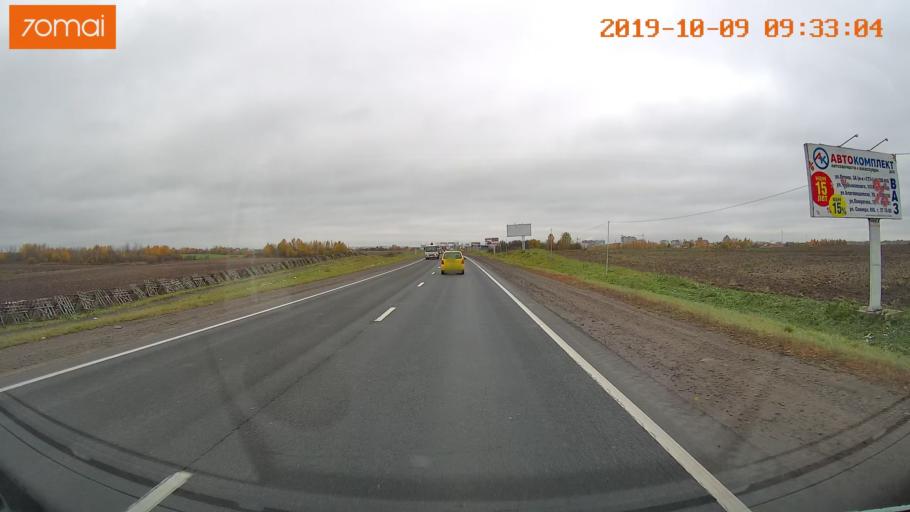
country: RU
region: Vologda
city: Vologda
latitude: 59.1650
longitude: 39.9200
